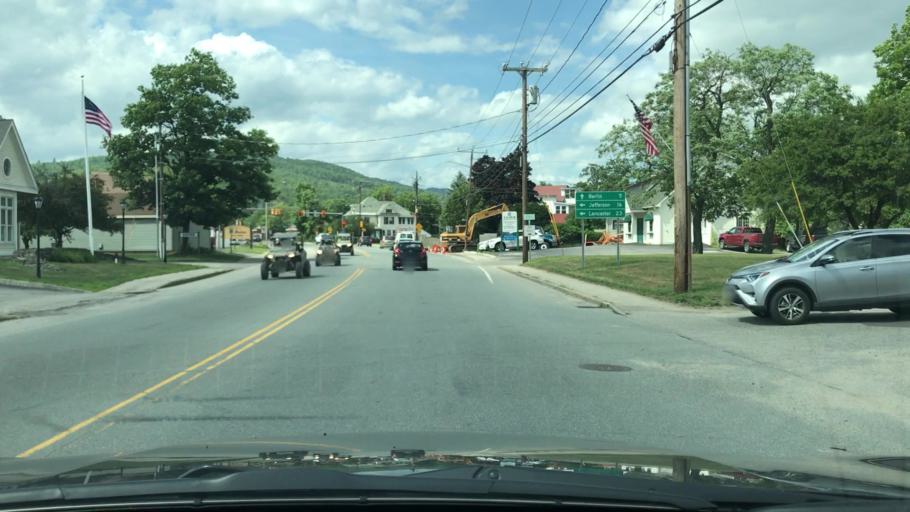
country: US
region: New Hampshire
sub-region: Coos County
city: Gorham
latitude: 44.3968
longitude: -71.1944
